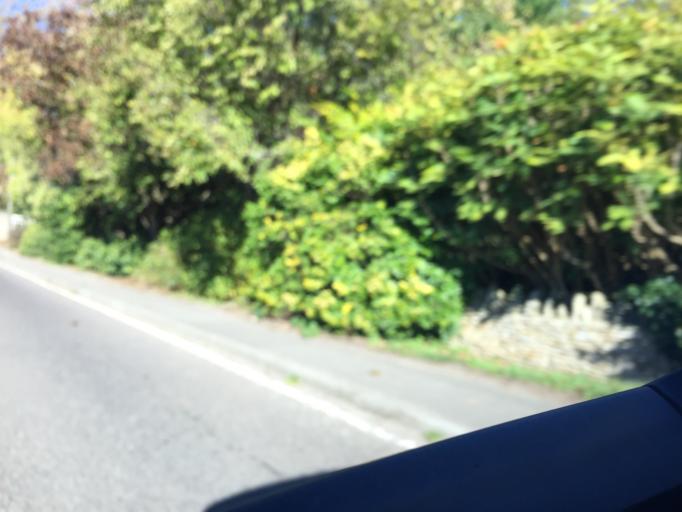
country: GB
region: England
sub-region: Wiltshire
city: Biddestone
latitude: 51.4725
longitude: -2.2277
